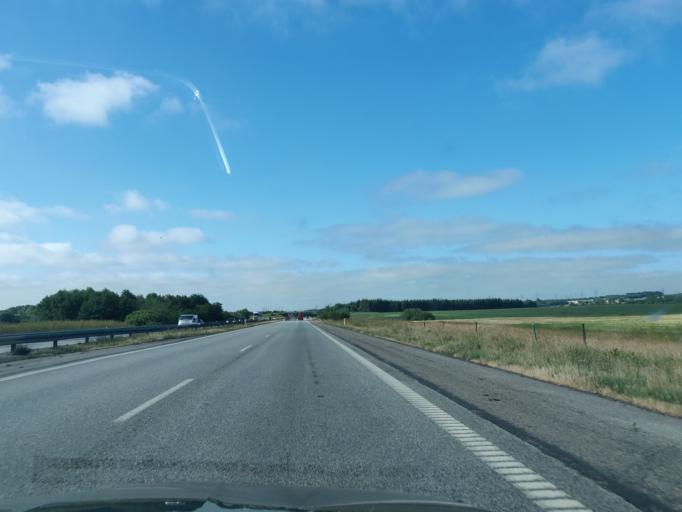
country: DK
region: North Denmark
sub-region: Alborg Kommune
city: Svenstrup
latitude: 56.9703
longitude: 9.8774
